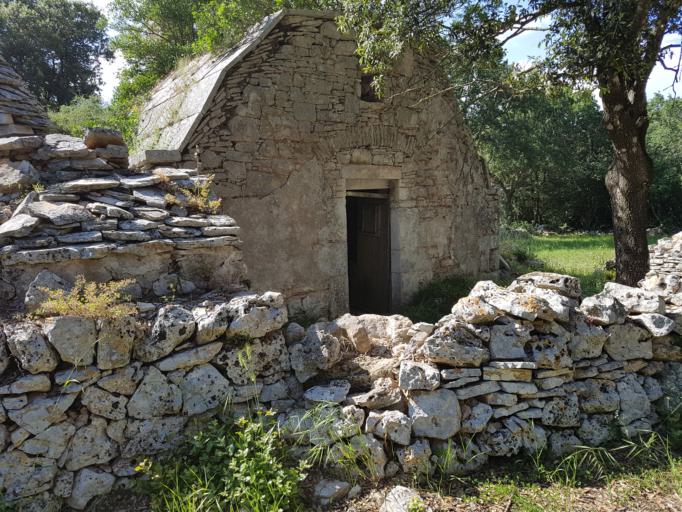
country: IT
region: Apulia
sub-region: Provincia di Taranto
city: Crispiano
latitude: 40.6606
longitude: 17.2375
